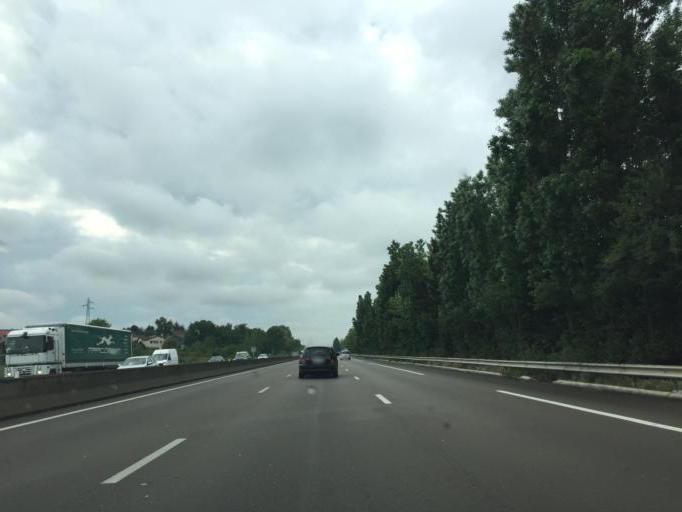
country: FR
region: Rhone-Alpes
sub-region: Departement de l'Isere
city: Salaise-sur-Sanne
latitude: 45.3474
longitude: 4.8067
